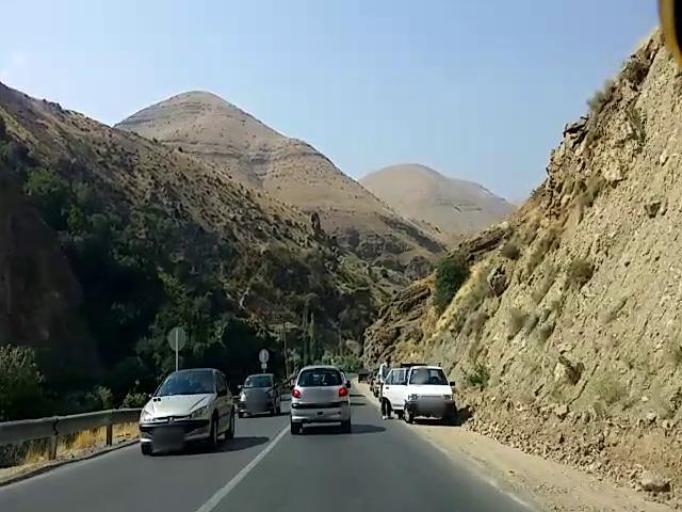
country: IR
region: Alborz
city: Karaj
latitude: 35.9190
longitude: 51.0501
